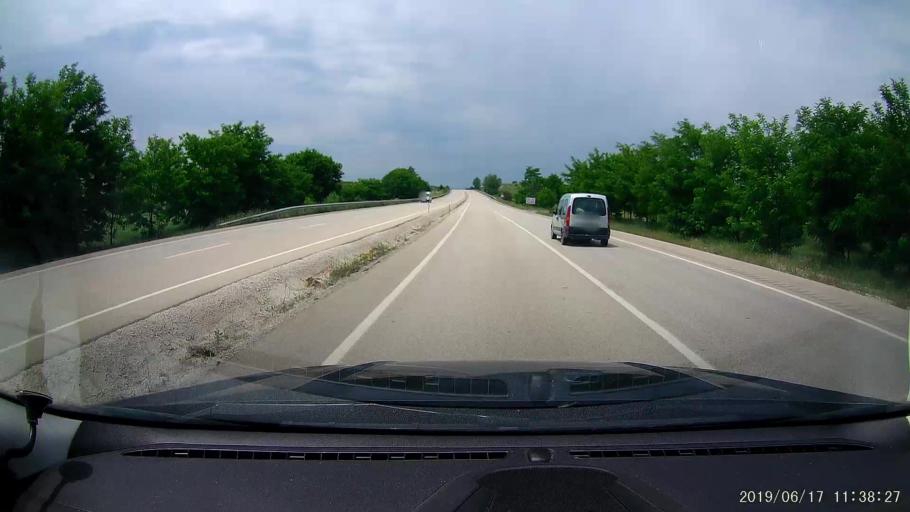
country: TR
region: Cankiri
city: Beloren
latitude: 40.8477
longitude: 33.3988
